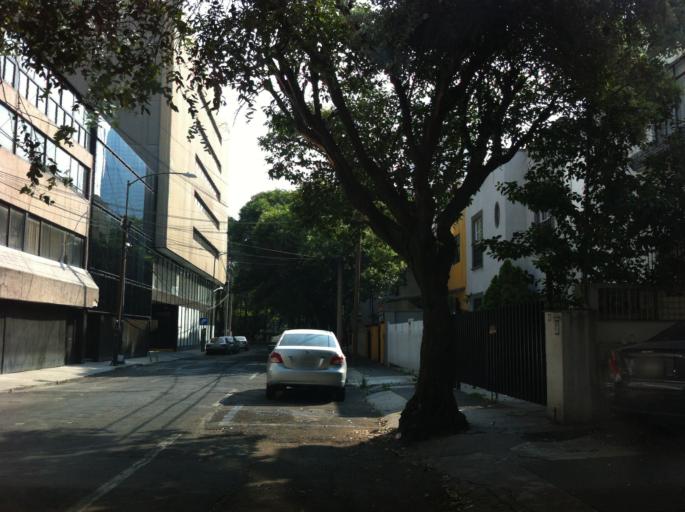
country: MX
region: Mexico City
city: Miguel Hidalgo
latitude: 19.4367
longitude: -99.1810
